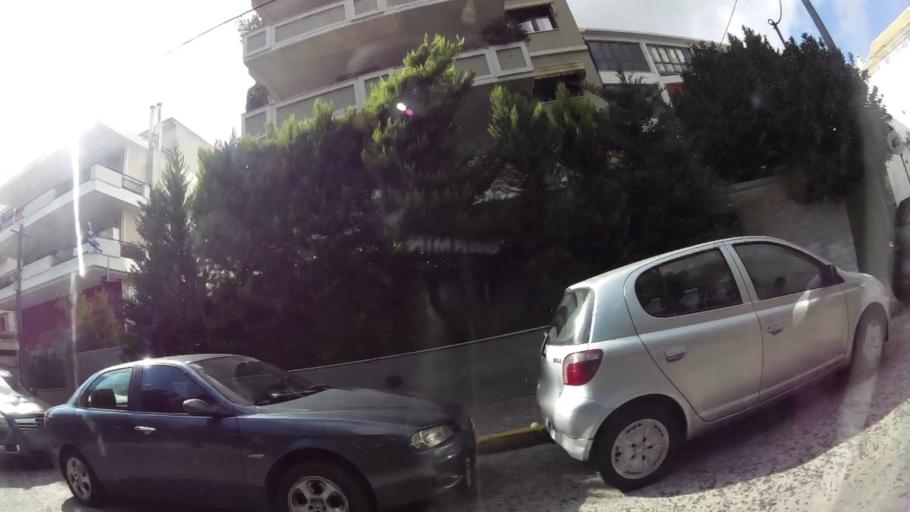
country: GR
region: Attica
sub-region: Nomarchia Athinas
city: Melissia
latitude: 38.0553
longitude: 23.8406
